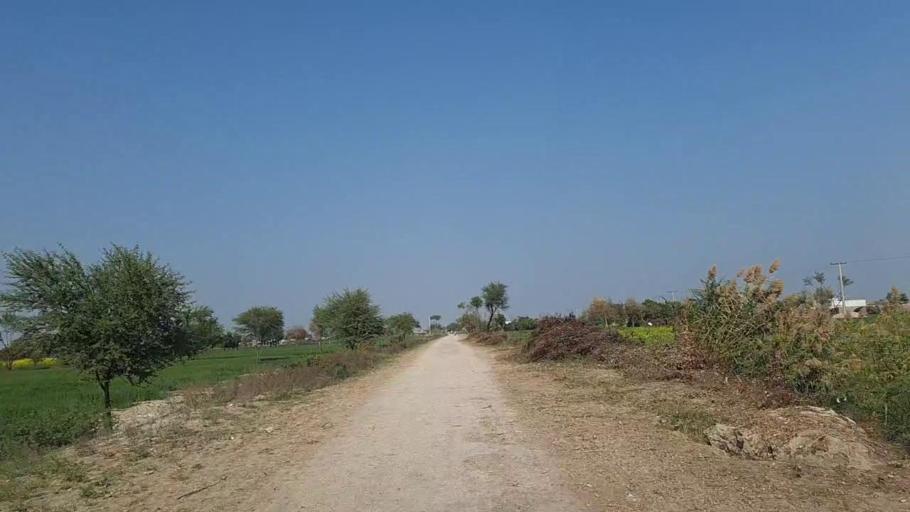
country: PK
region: Sindh
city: Nawabshah
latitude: 26.2828
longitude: 68.5136
